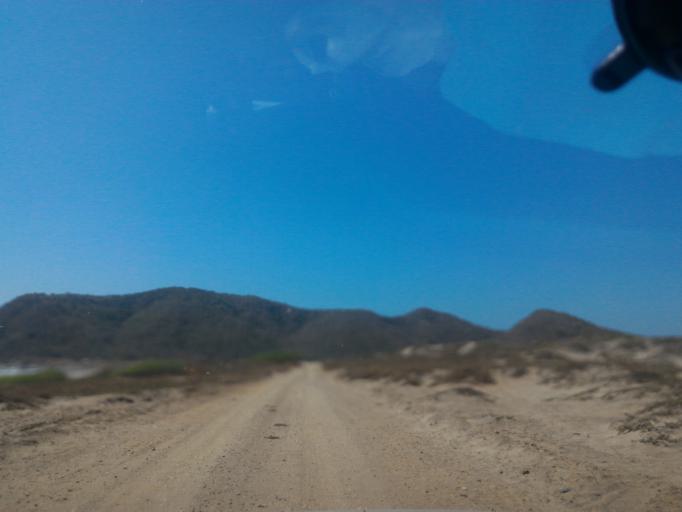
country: MX
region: Michoacan
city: Coahuayana Viejo
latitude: 18.5931
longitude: -103.6938
